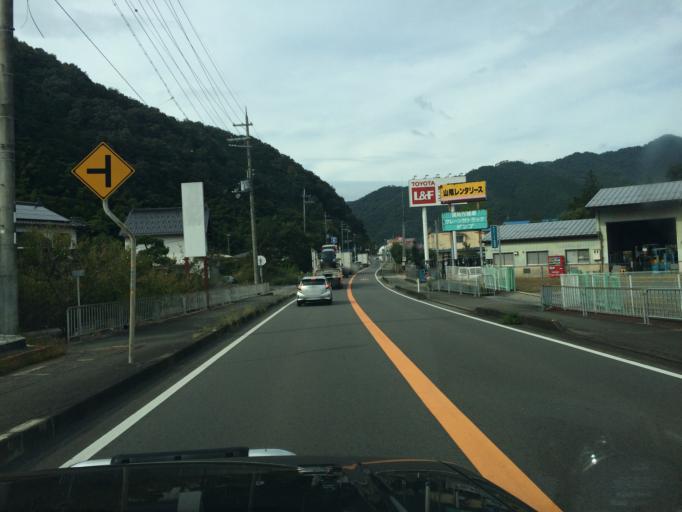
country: JP
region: Hyogo
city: Toyooka
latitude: 35.3494
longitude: 134.8361
